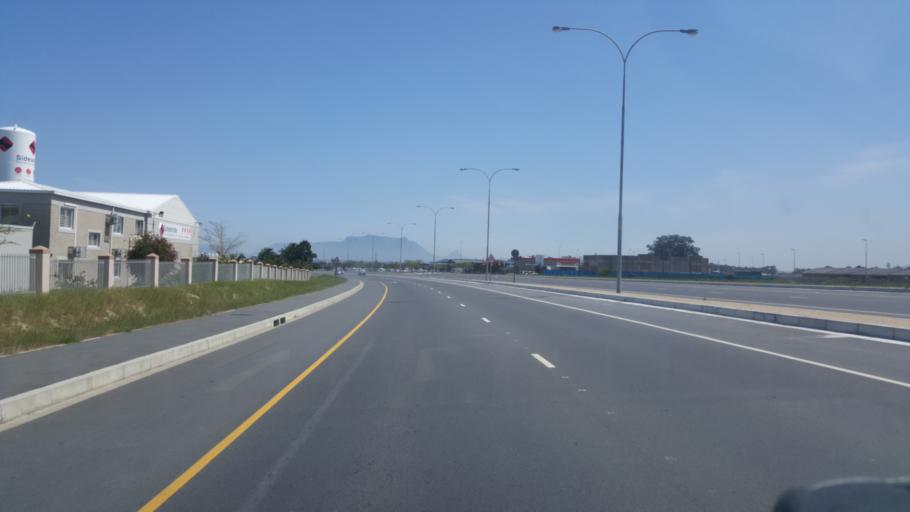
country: ZA
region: Western Cape
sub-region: City of Cape Town
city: Kraaifontein
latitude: -33.9495
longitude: 18.7029
